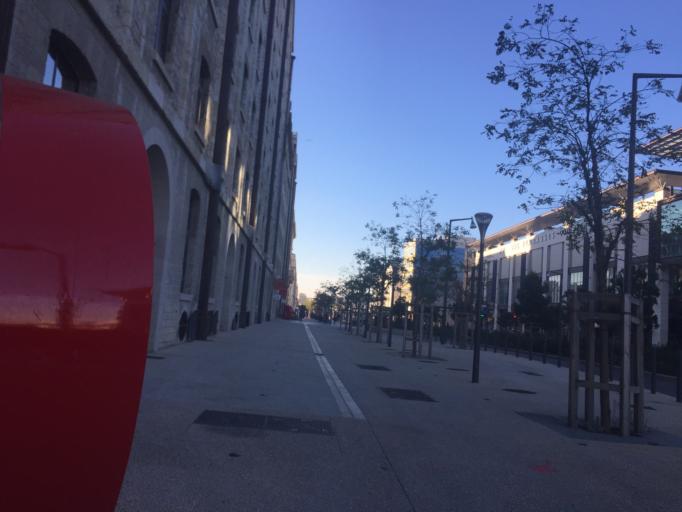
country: FR
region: Provence-Alpes-Cote d'Azur
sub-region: Departement des Bouches-du-Rhone
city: Marseille 03
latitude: 43.3068
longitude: 5.3659
